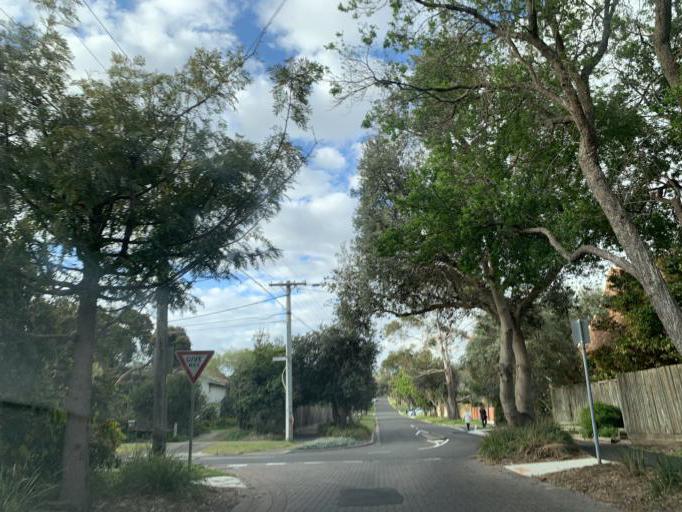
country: AU
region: Victoria
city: Beaumaris
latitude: -37.9801
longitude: 145.0248
